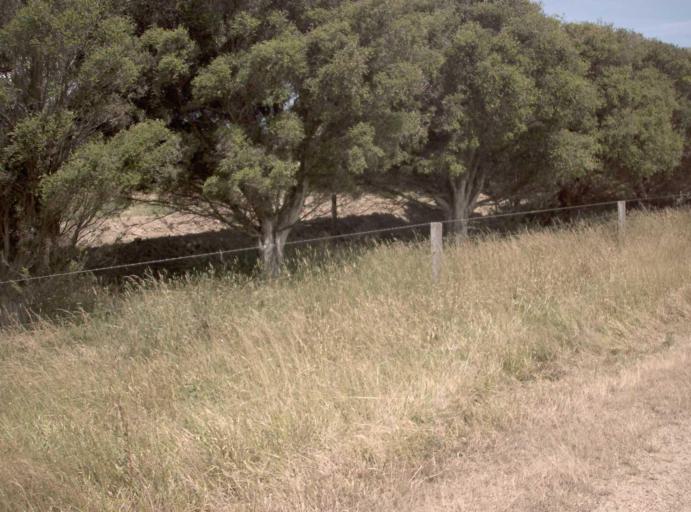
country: AU
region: Victoria
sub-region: Wellington
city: Heyfield
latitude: -38.0616
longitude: 146.8726
